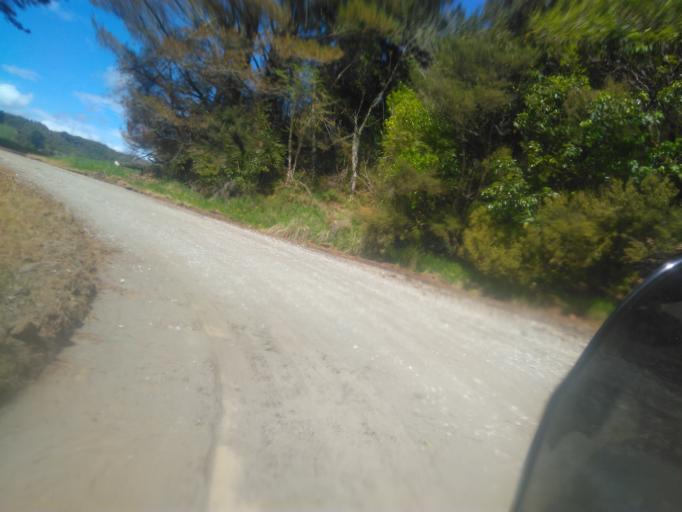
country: NZ
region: Hawke's Bay
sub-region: Wairoa District
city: Wairoa
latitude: -38.7759
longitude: 177.6082
